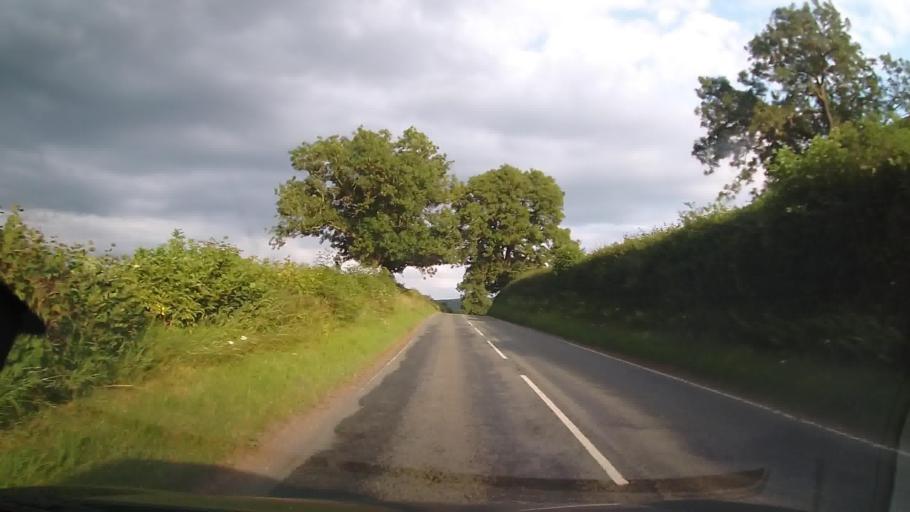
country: GB
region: Wales
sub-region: Sir Powys
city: Llangynog
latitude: 52.8201
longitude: -3.3768
